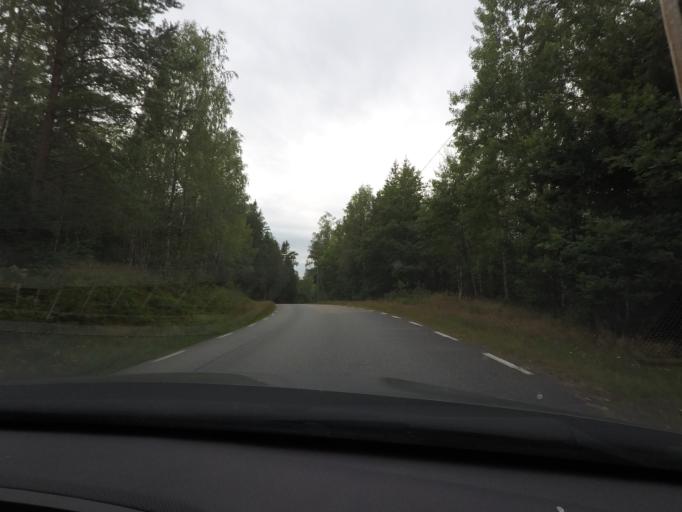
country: SE
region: Skane
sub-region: Osby Kommun
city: Osby
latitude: 56.4252
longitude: 13.8456
